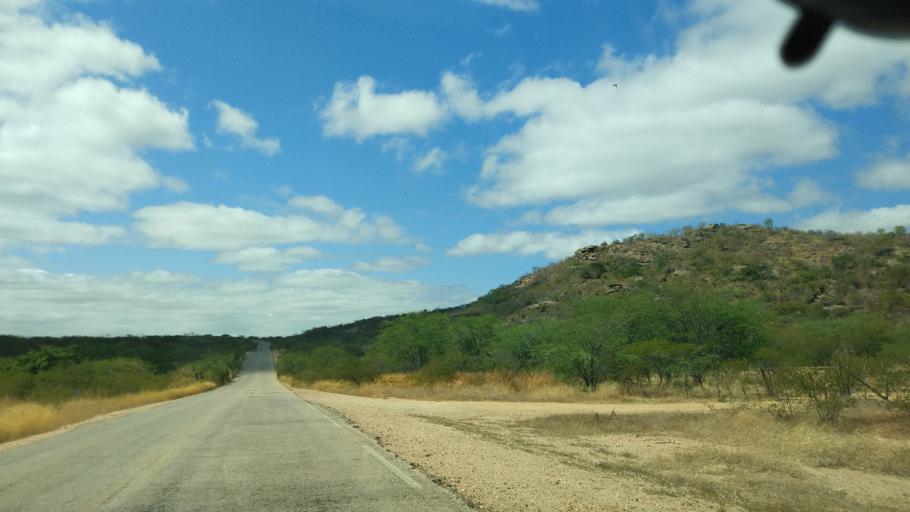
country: BR
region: Rio Grande do Norte
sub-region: Currais Novos
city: Currais Novos
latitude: -6.2669
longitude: -36.5615
